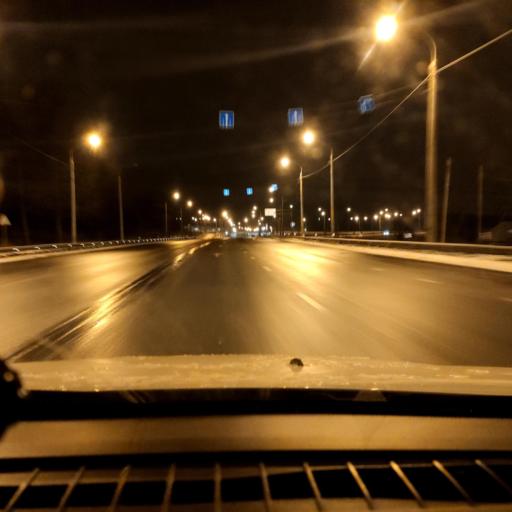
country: RU
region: Samara
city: Volzhskiy
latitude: 53.4378
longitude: 50.1108
